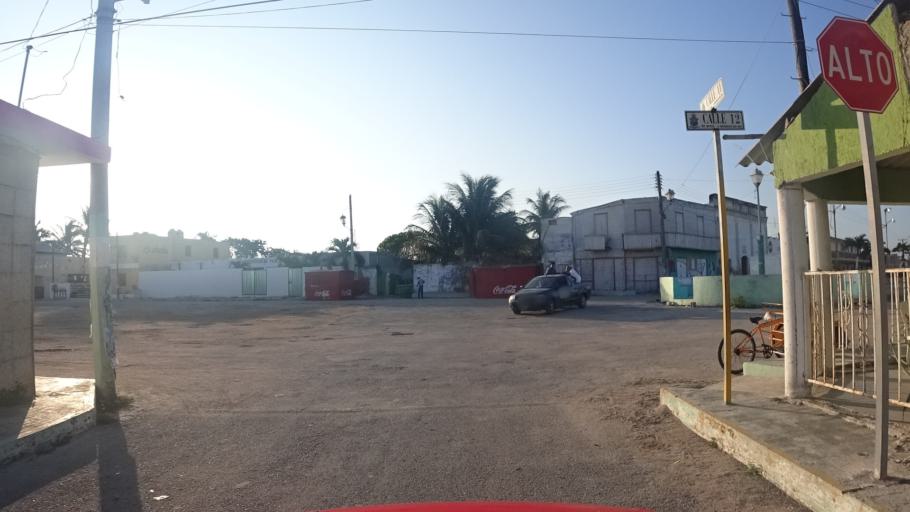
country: MX
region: Yucatan
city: Rio Lagartos
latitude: 21.5984
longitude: -88.1580
